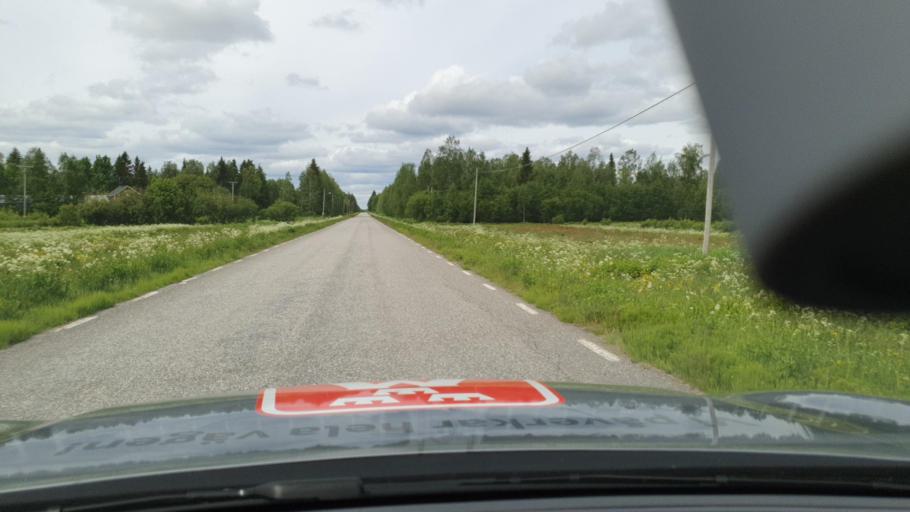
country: FI
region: Lapland
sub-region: Torniolaakso
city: Ylitornio
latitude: 66.0352
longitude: 23.8053
